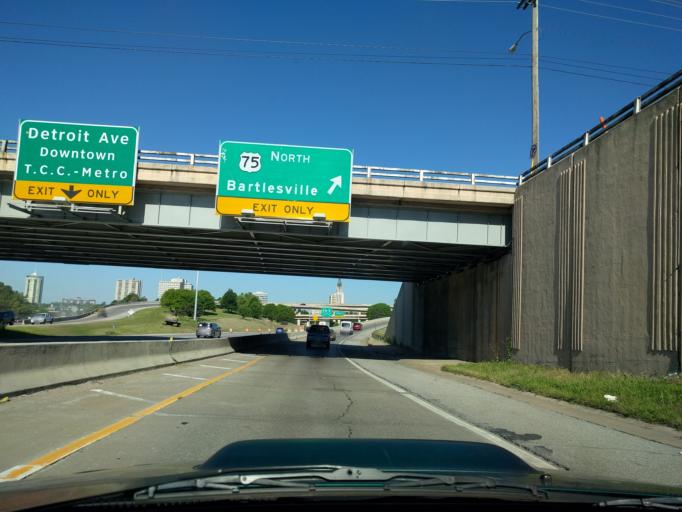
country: US
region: Oklahoma
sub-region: Tulsa County
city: Tulsa
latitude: 36.1432
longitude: -95.9752
